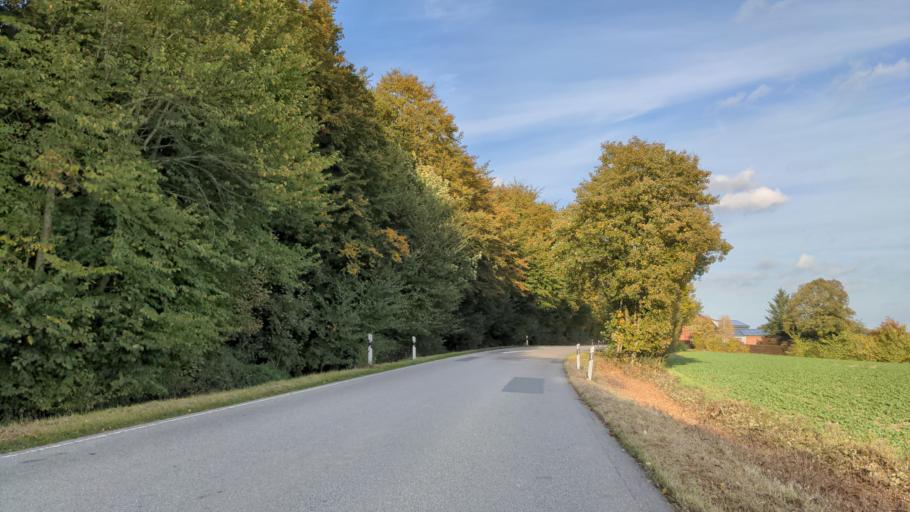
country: DE
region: Schleswig-Holstein
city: Ahrensbok
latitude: 53.9852
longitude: 10.5682
